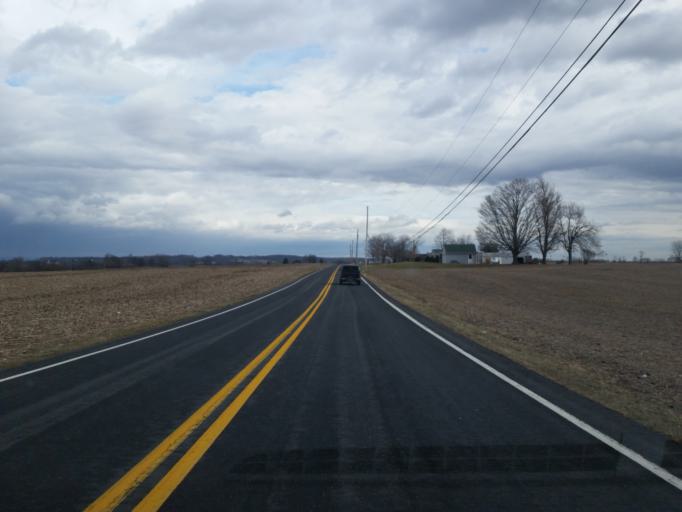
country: US
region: Pennsylvania
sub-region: Lebanon County
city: Palmyra
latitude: 40.3070
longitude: -76.5606
